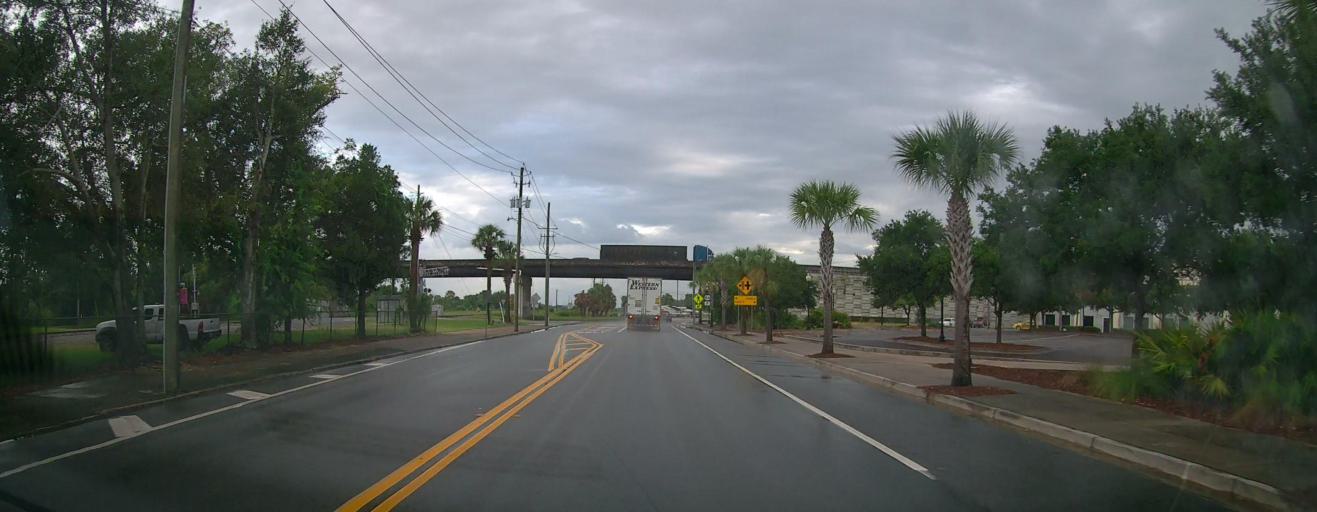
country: US
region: Georgia
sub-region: Ware County
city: Waycross
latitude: 31.2085
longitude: -82.3597
